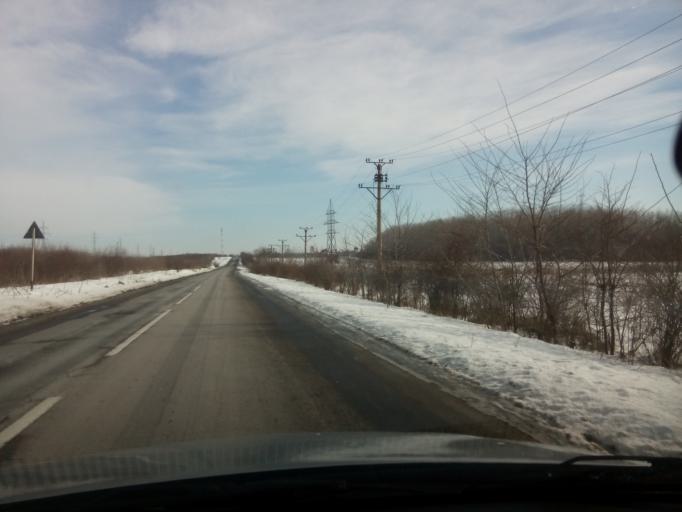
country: RO
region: Calarasi
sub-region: Comuna Budesti
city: Budesti
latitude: 44.2319
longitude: 26.4763
